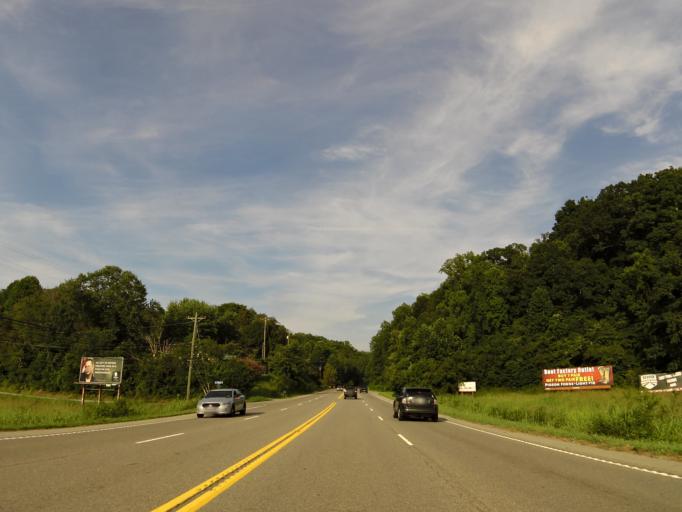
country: US
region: Tennessee
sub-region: Sevier County
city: Seymour
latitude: 35.8480
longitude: -83.7068
